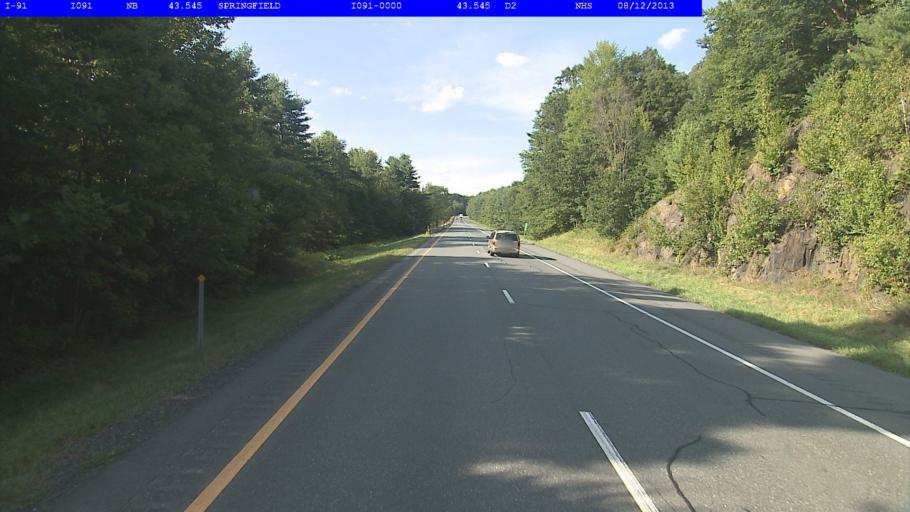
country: US
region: New Hampshire
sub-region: Sullivan County
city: Charlestown
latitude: 43.2920
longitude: -72.4270
